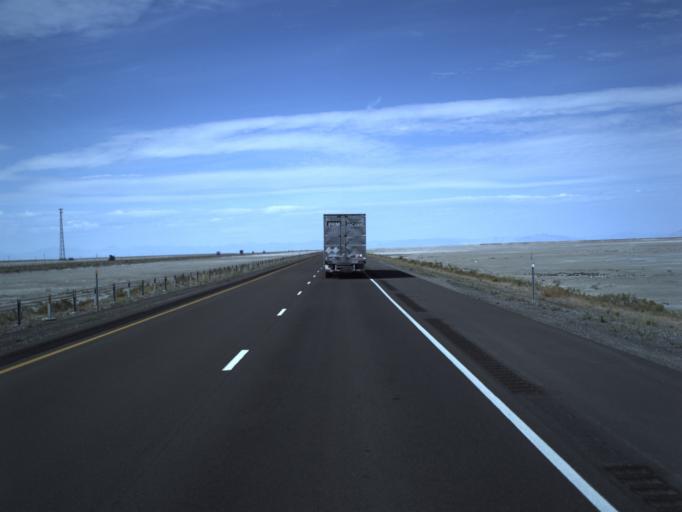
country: US
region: Utah
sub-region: Tooele County
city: Wendover
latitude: 40.7283
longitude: -113.3166
